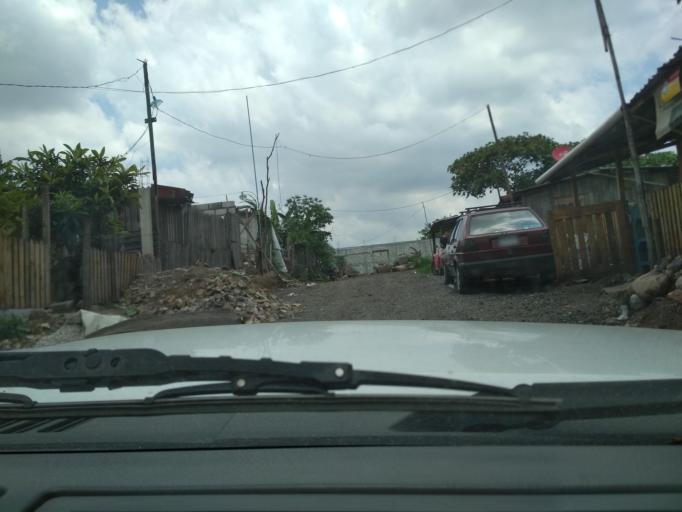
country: MX
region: Veracruz
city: Cordoba
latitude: 18.8857
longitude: -96.9187
